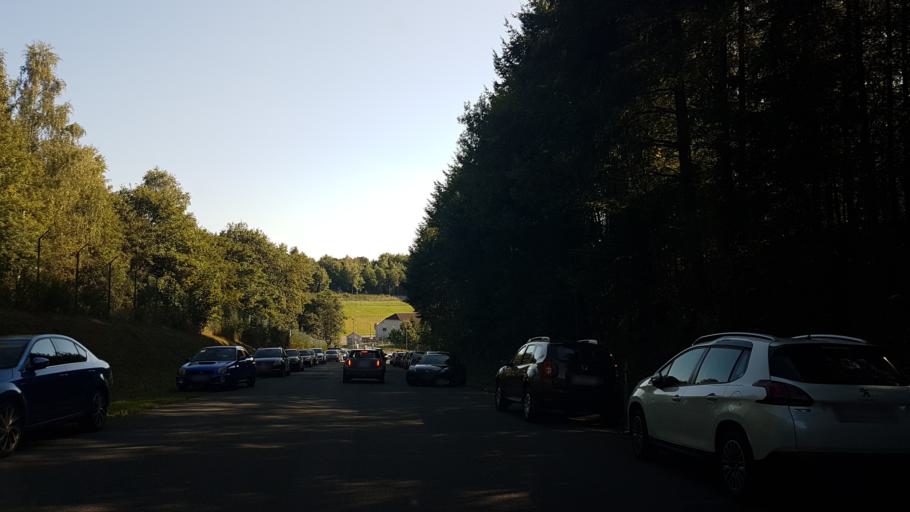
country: DE
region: Rheinland-Pfalz
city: Baumholder
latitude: 49.6278
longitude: 7.3149
